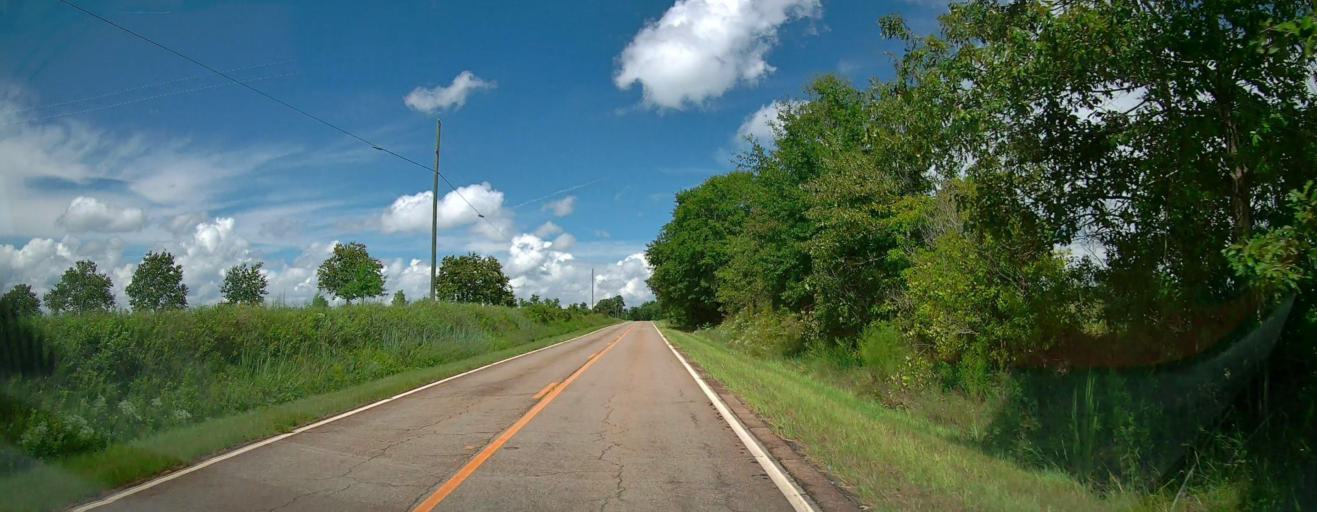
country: US
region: Georgia
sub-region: Peach County
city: Fort Valley
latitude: 32.5281
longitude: -83.8026
